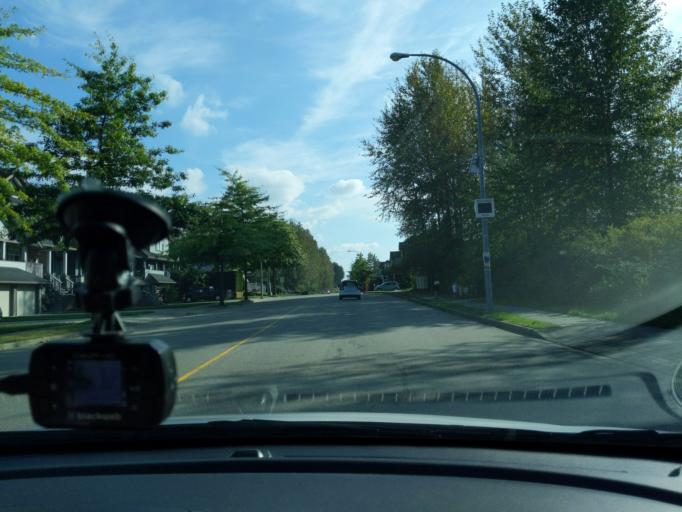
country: CA
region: British Columbia
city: Pitt Meadows
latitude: 49.2067
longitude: -122.6784
